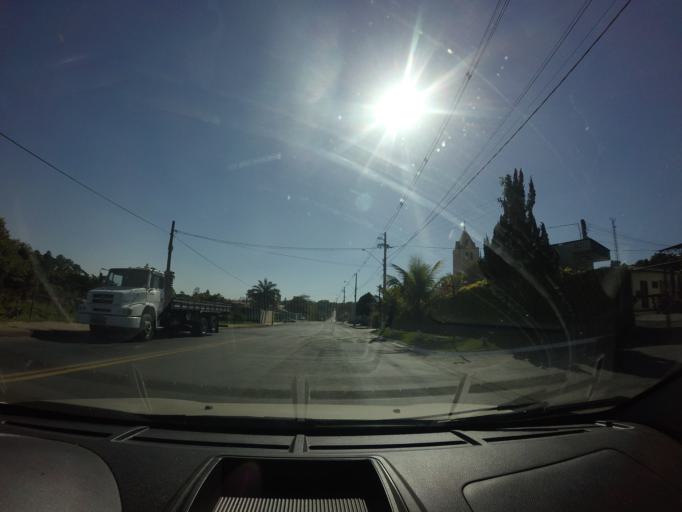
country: BR
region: Sao Paulo
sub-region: Piracicaba
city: Piracicaba
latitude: -22.7520
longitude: -47.6121
